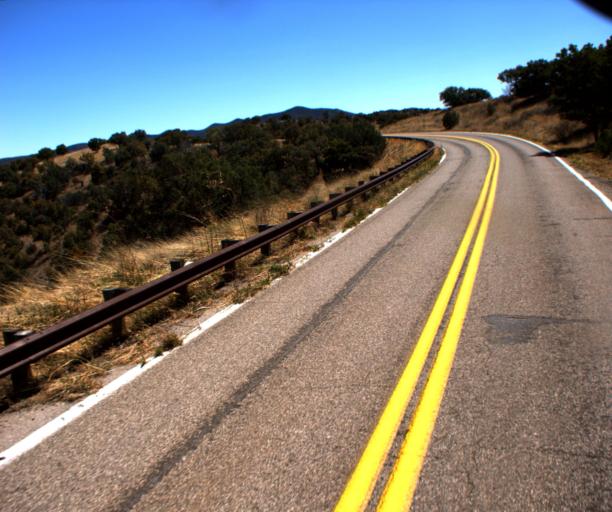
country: US
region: Arizona
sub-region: Cochise County
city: Sierra Vista
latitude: 31.5171
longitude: -110.4979
